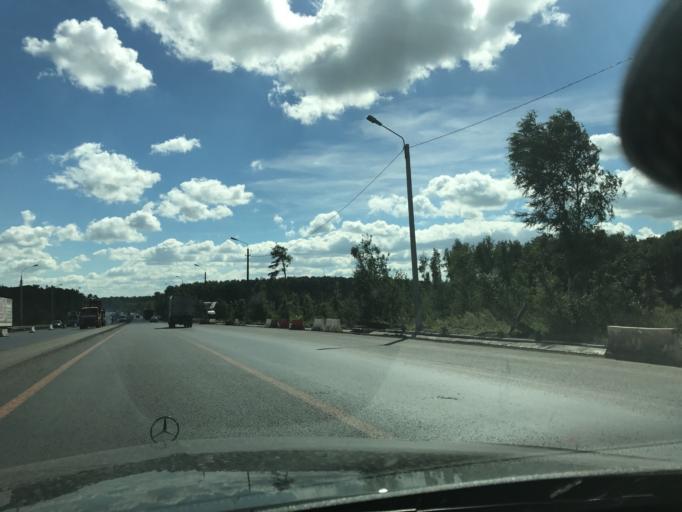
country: RU
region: Nizjnij Novgorod
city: Gorbatovka
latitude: 56.2578
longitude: 43.7094
